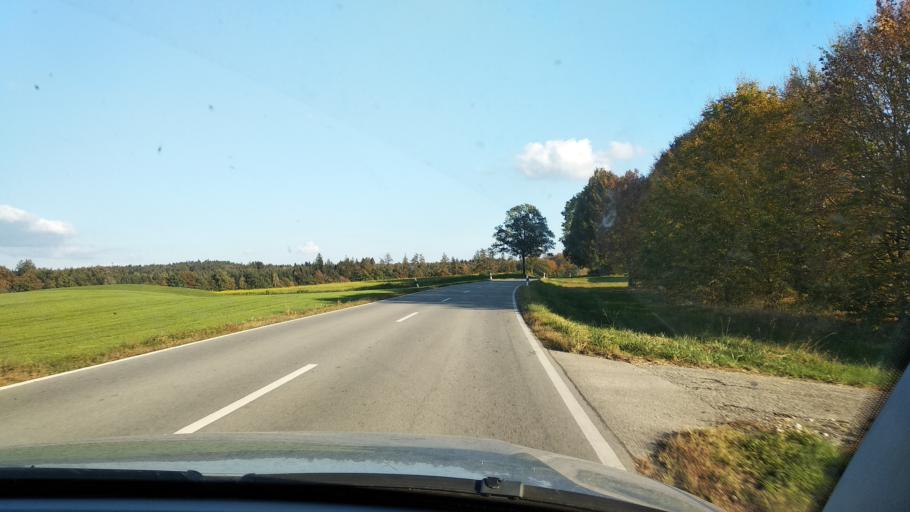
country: DE
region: Bavaria
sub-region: Upper Bavaria
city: Egmating
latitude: 48.0047
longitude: 11.8036
